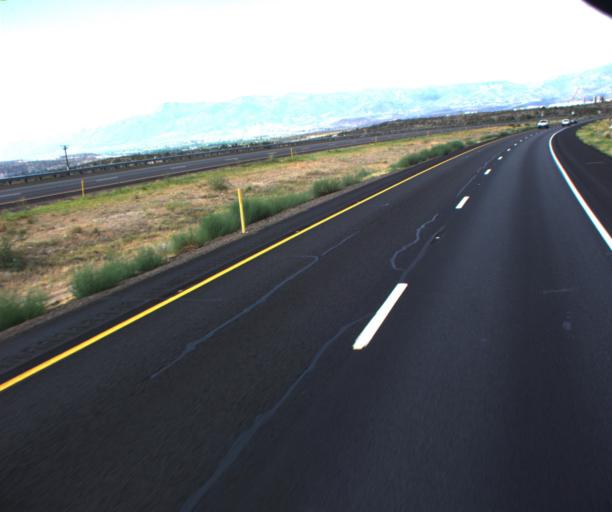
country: US
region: Arizona
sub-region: Yavapai County
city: Camp Verde
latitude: 34.6170
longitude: -111.8477
